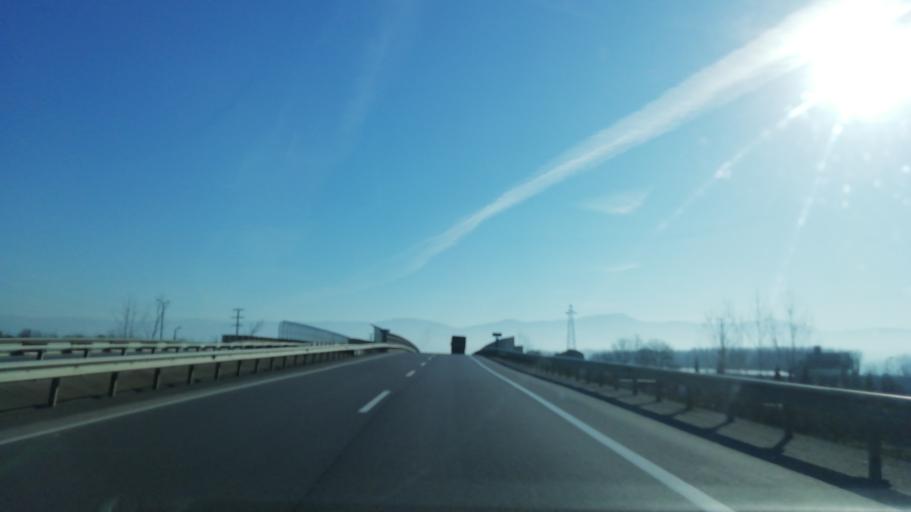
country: TR
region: Sakarya
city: Akyazi
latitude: 40.7179
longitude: 30.5631
